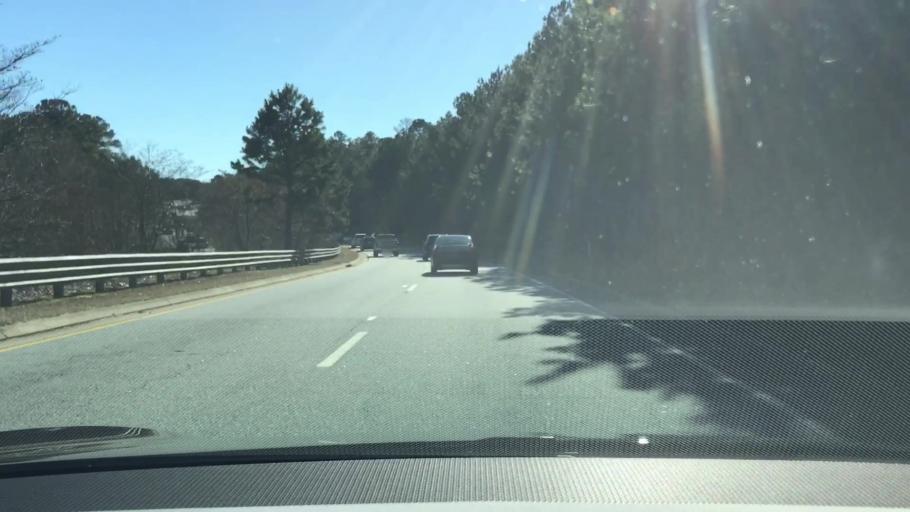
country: US
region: Georgia
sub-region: Gwinnett County
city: Suwanee
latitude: 34.0358
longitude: -84.0719
